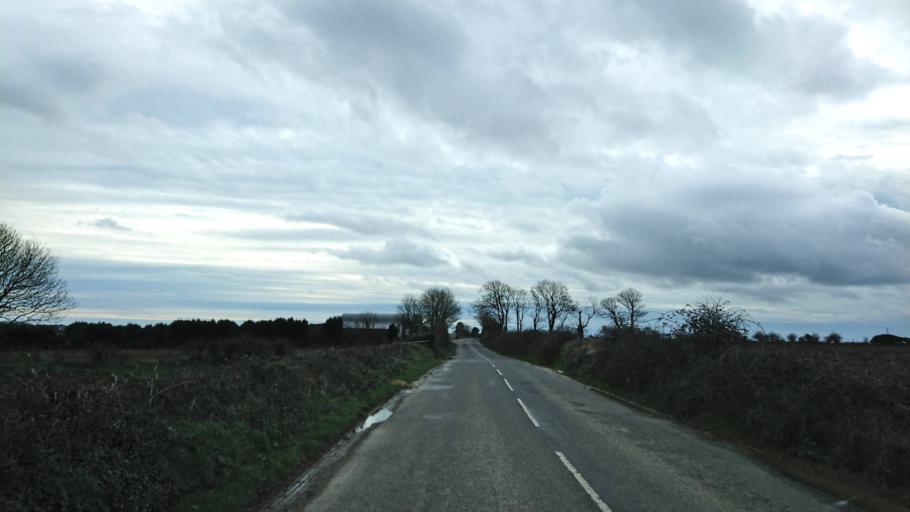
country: IE
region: Munster
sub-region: Waterford
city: Dunmore East
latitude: 52.2435
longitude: -6.9079
